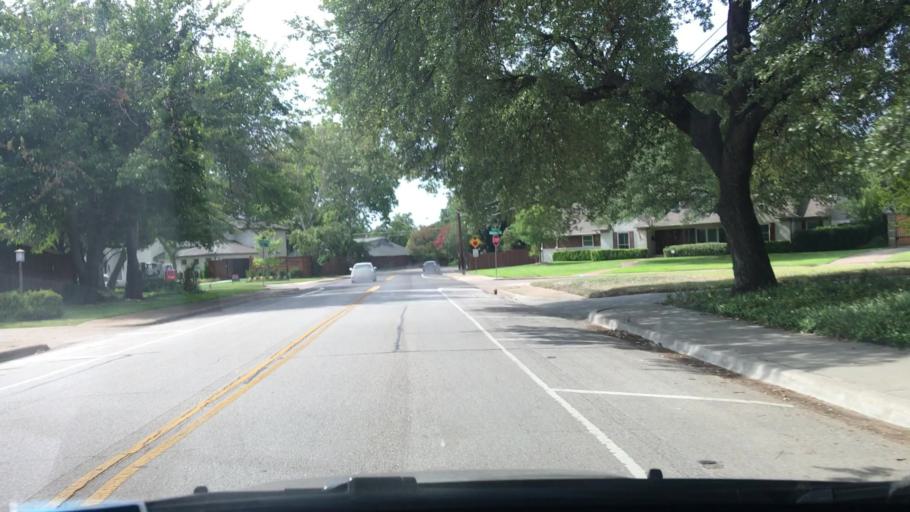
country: US
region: Texas
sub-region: Dallas County
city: Addison
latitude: 32.9103
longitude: -96.8107
